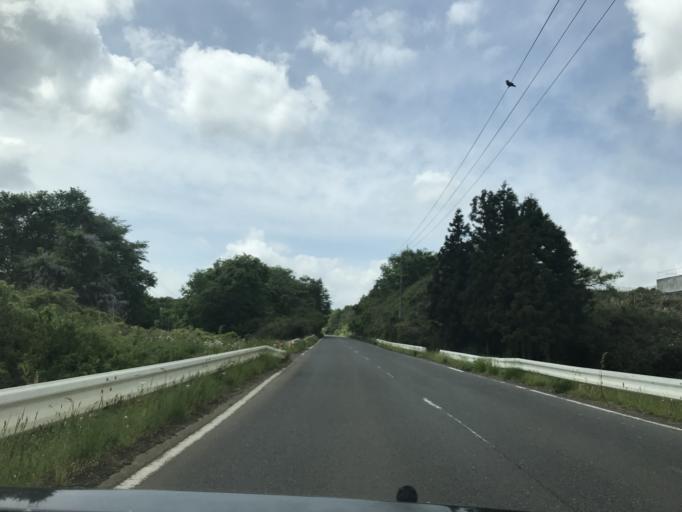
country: JP
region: Iwate
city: Ichinoseki
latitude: 38.8085
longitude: 141.0125
